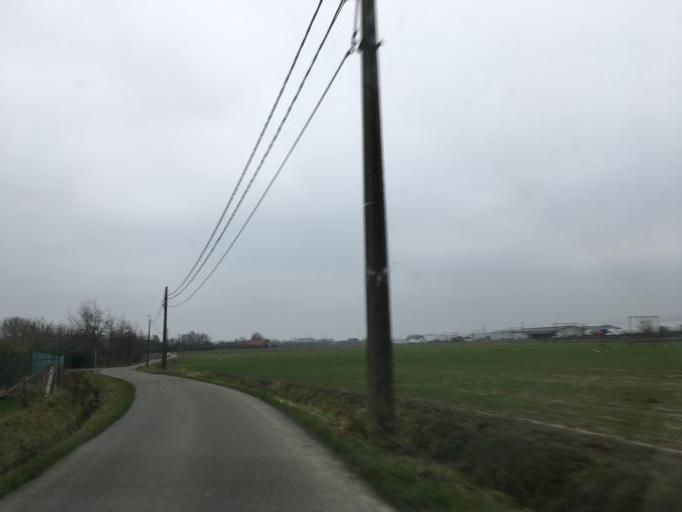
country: BE
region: Flanders
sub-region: Provincie West-Vlaanderen
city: Hooglede
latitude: 50.9901
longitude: 3.1228
